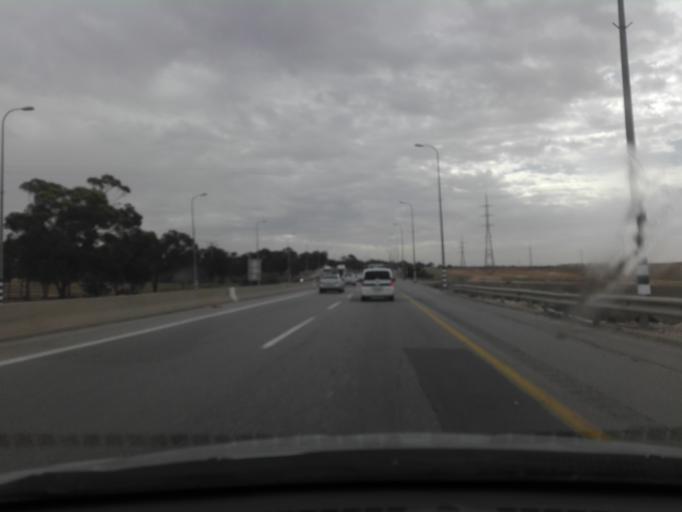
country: IL
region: Southern District
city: Lehavim
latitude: 31.3676
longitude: 34.7950
